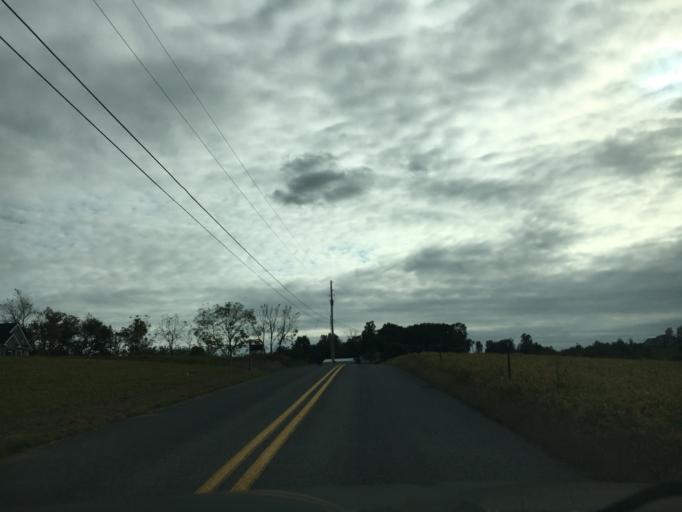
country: US
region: Pennsylvania
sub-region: Lehigh County
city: Schnecksville
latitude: 40.6249
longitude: -75.6815
